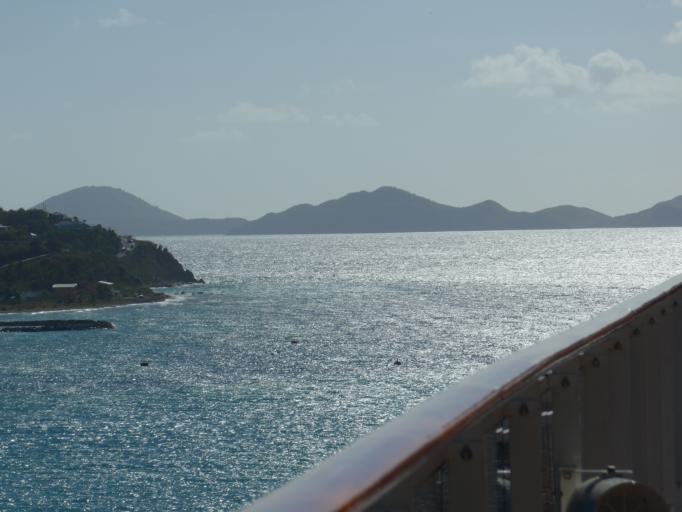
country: VG
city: Road Town
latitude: 18.4225
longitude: -64.6128
